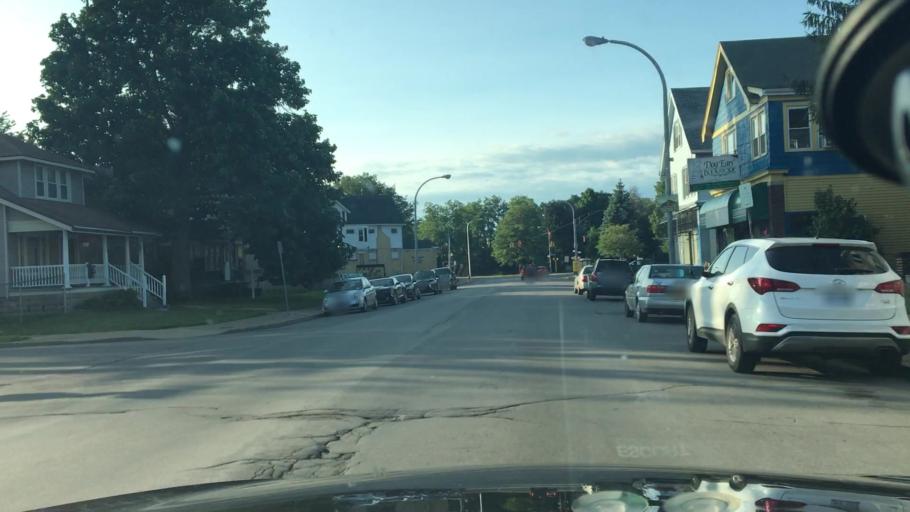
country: US
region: New York
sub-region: Erie County
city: West Seneca
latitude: 42.8452
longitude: -78.8097
